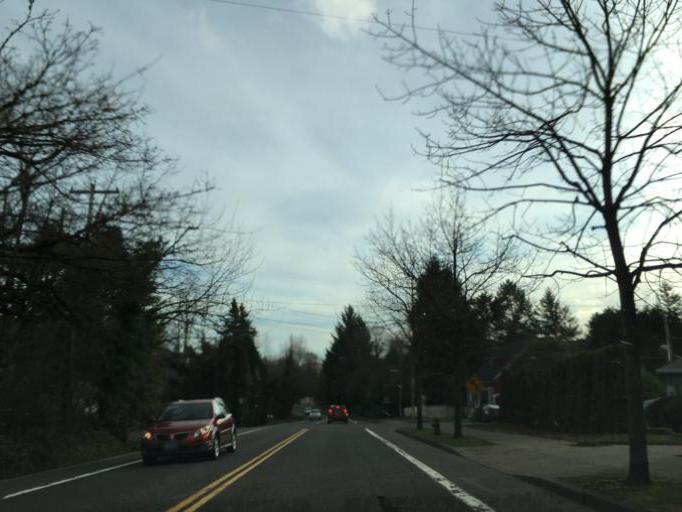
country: US
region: Oregon
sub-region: Clackamas County
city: Lake Oswego
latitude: 45.4579
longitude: -122.6850
